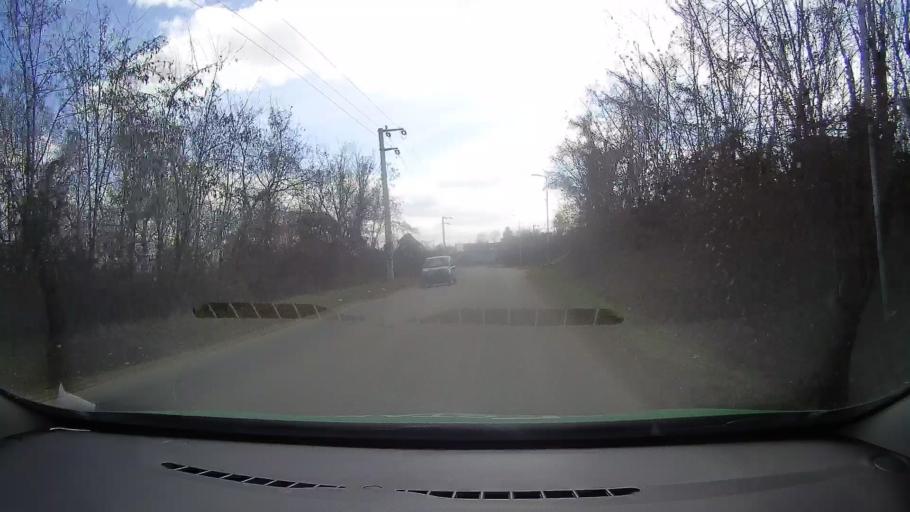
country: RO
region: Dambovita
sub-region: Comuna Sotanga
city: Teis
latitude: 44.9688
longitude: 25.3972
